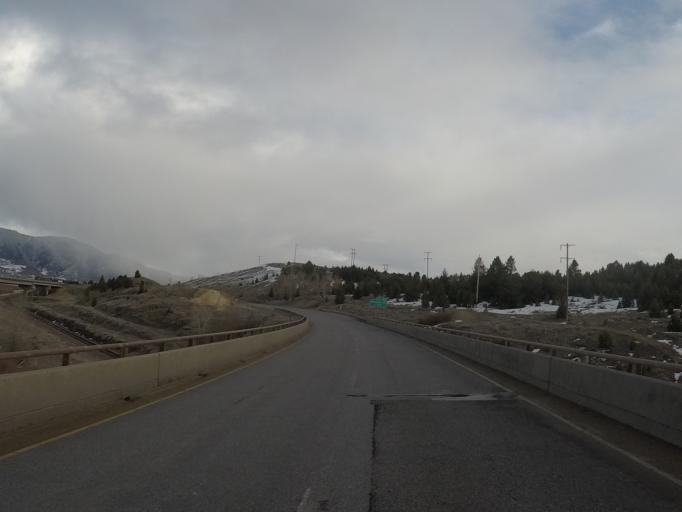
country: US
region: Montana
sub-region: Silver Bow County
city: Butte
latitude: 45.9971
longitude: -112.5668
